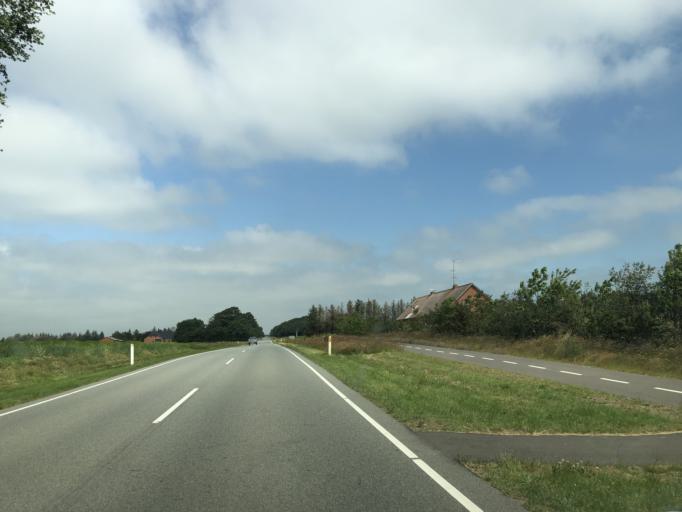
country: DK
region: South Denmark
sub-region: Varde Kommune
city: Varde
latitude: 55.6435
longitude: 8.4869
